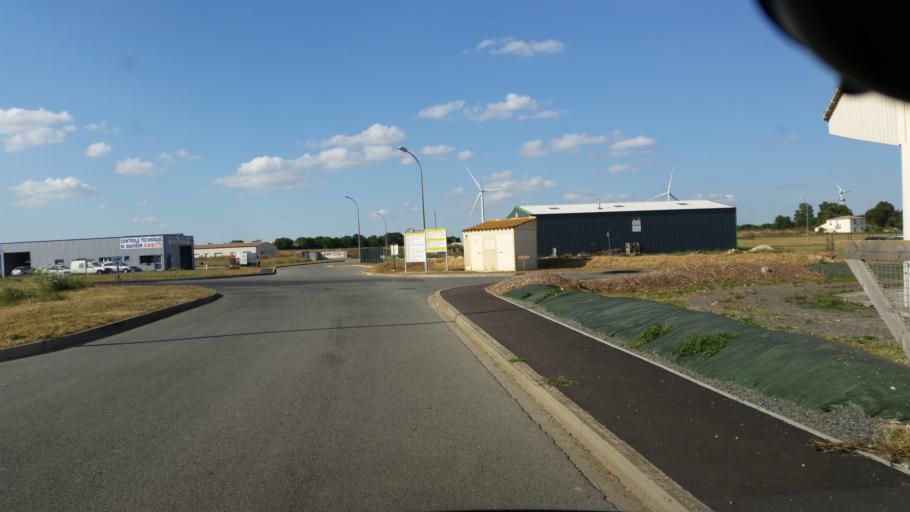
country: FR
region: Poitou-Charentes
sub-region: Departement de la Charente-Maritime
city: Saint-Jean-de-Liversay
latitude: 46.2319
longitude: -0.8847
